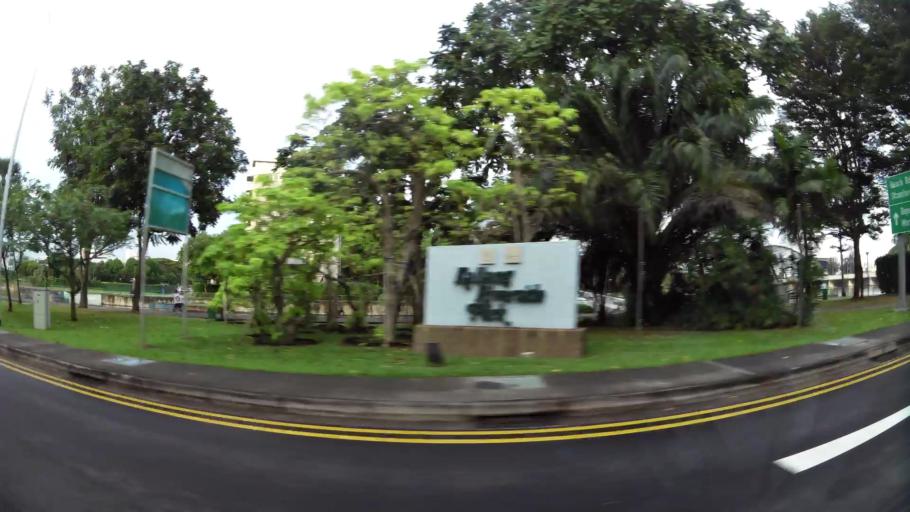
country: SG
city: Singapore
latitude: 1.3052
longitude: 103.8657
